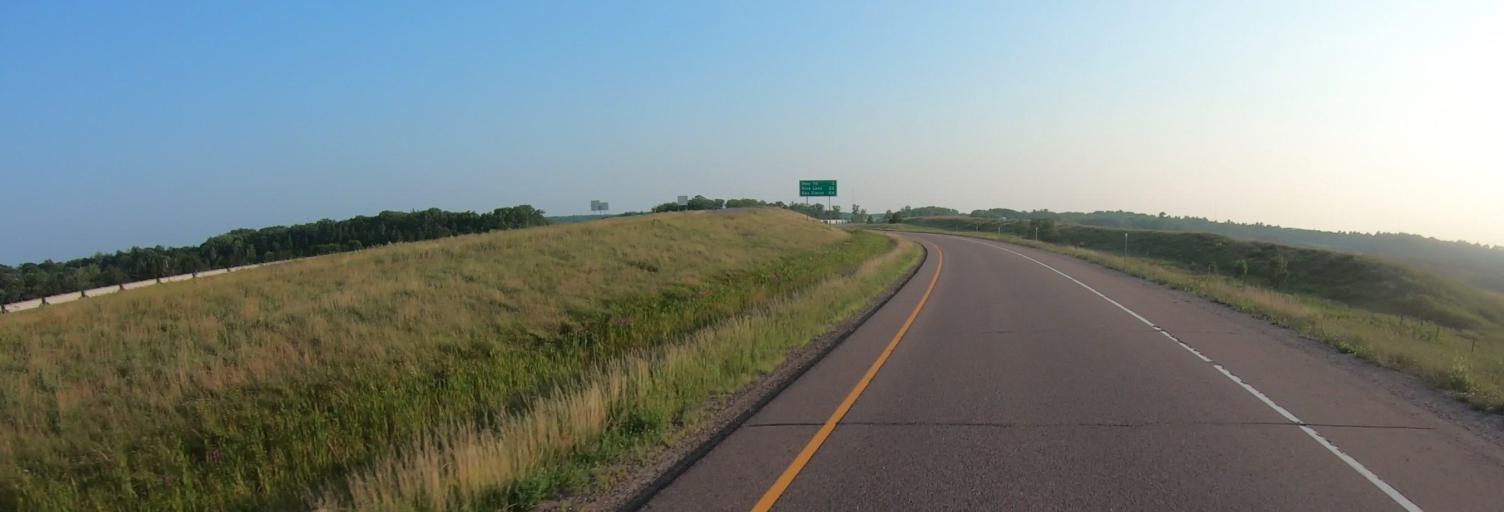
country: US
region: Wisconsin
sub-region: Washburn County
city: Spooner
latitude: 45.8553
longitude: -91.8588
